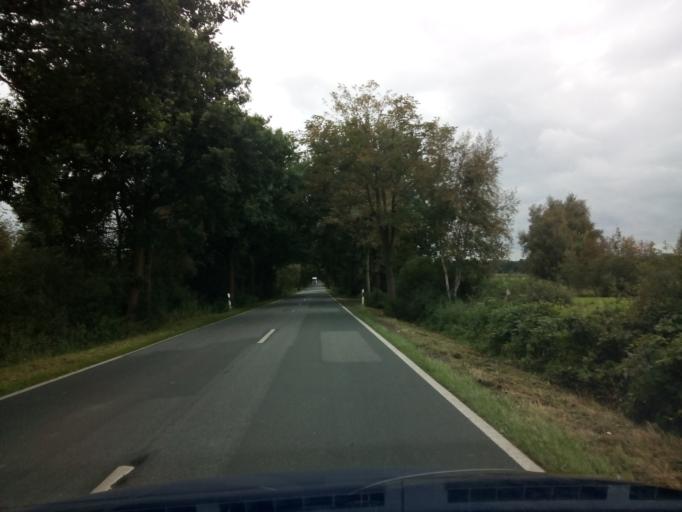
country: DE
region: Lower Saxony
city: Beverstedt
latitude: 53.4595
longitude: 8.8406
